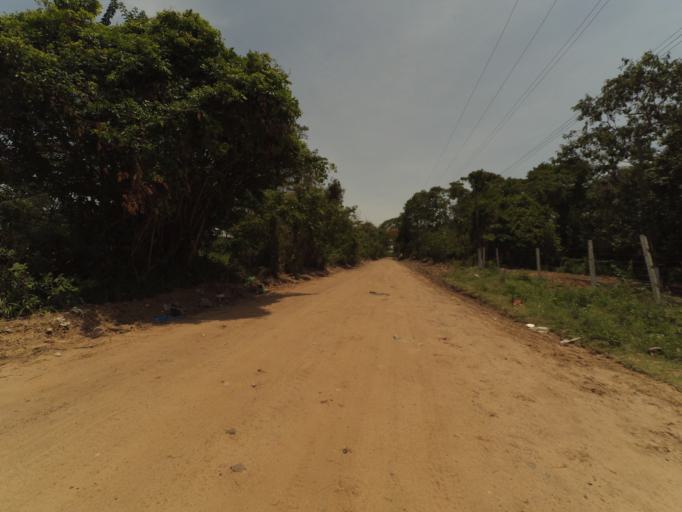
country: BO
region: Santa Cruz
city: Santa Cruz de la Sierra
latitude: -17.8275
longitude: -63.2526
